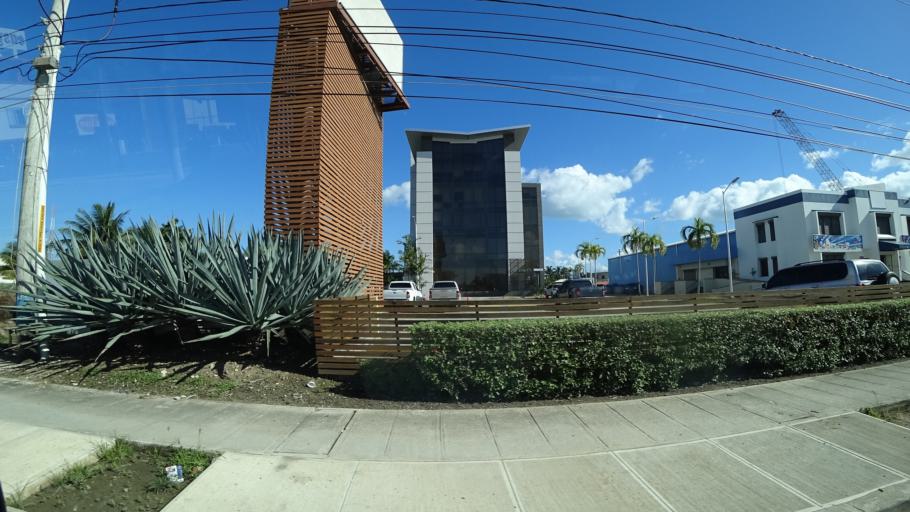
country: BZ
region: Belize
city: Belize City
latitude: 17.5080
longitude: -88.2049
